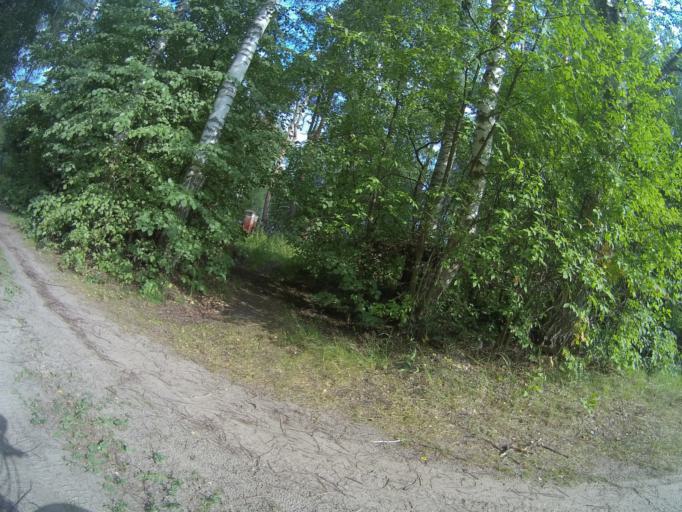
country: RU
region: Vladimir
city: Vorsha
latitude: 56.0097
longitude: 40.1462
